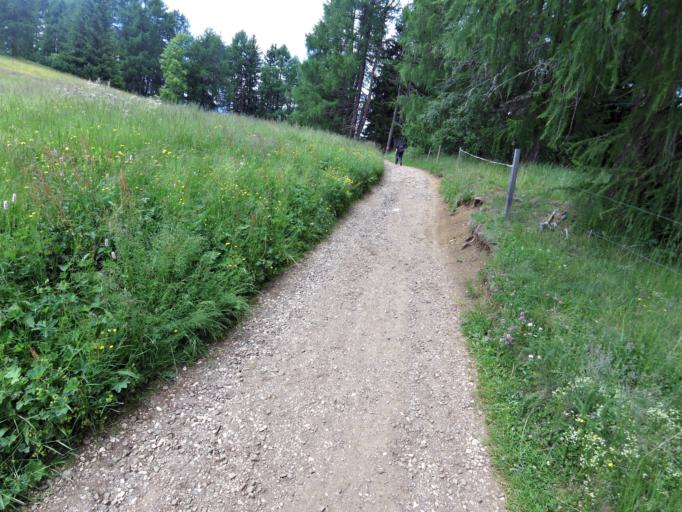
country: IT
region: Trentino-Alto Adige
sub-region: Bolzano
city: Ortisei
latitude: 46.5385
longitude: 11.6402
